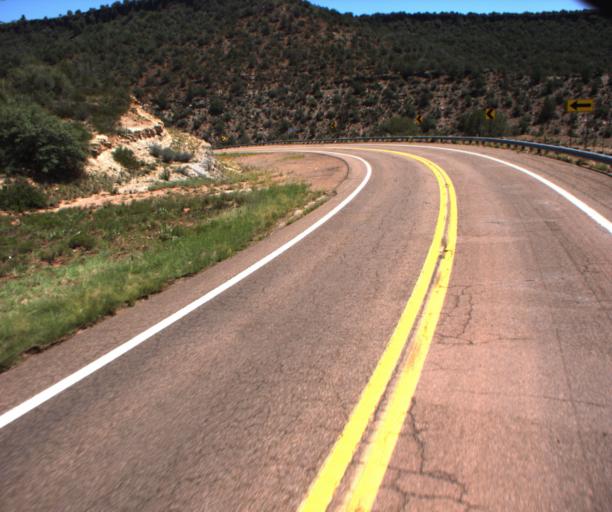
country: US
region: Arizona
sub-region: Navajo County
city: Cibecue
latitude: 33.9822
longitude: -110.2838
